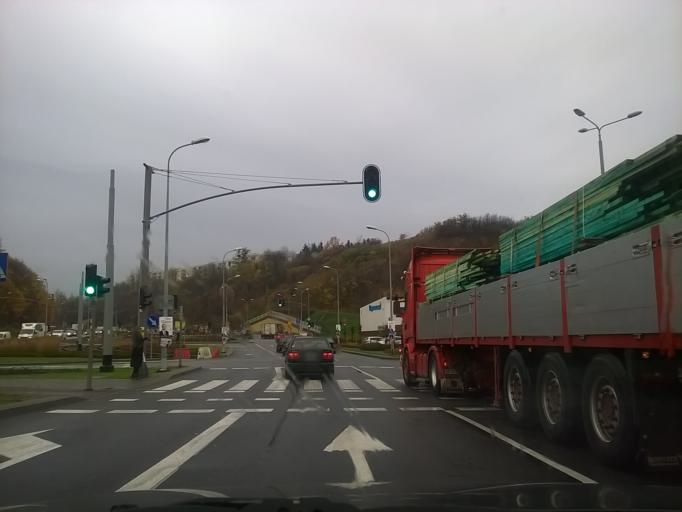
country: PL
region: Pomeranian Voivodeship
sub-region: Gdansk
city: Gdansk
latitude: 54.3470
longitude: 18.6035
